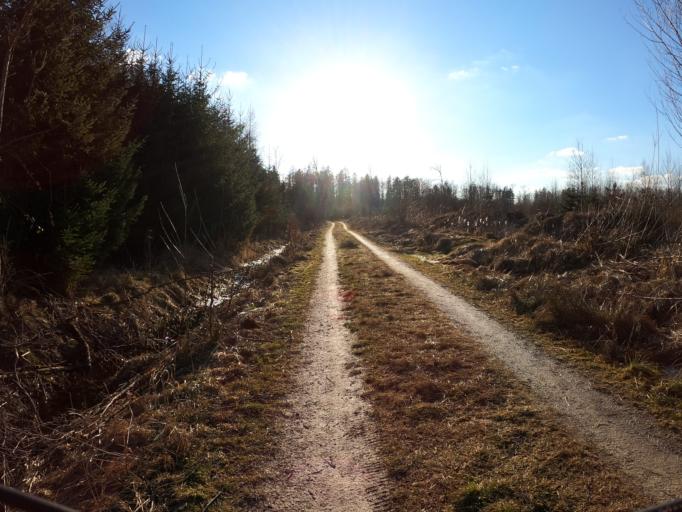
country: DE
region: Bavaria
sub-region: Swabia
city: Leipheim
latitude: 48.4173
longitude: 10.2120
